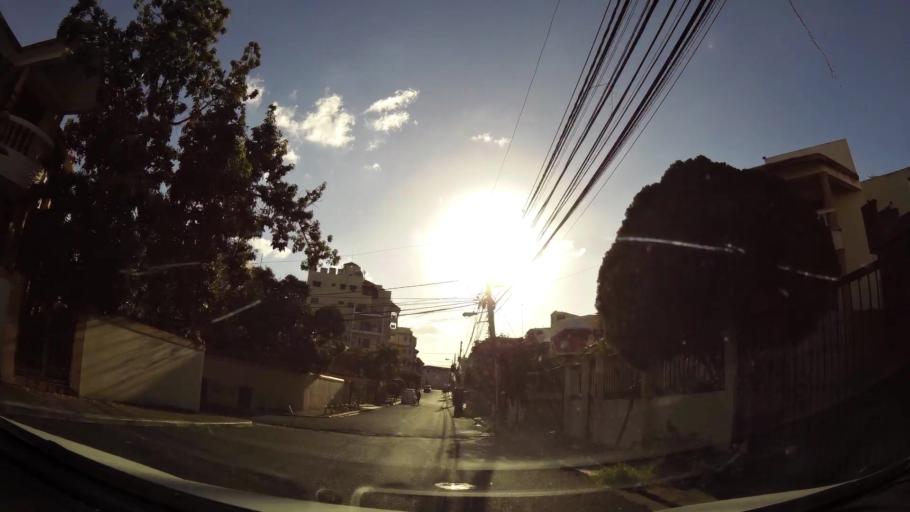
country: DO
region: Nacional
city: Santo Domingo
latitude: 18.4918
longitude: -69.9740
